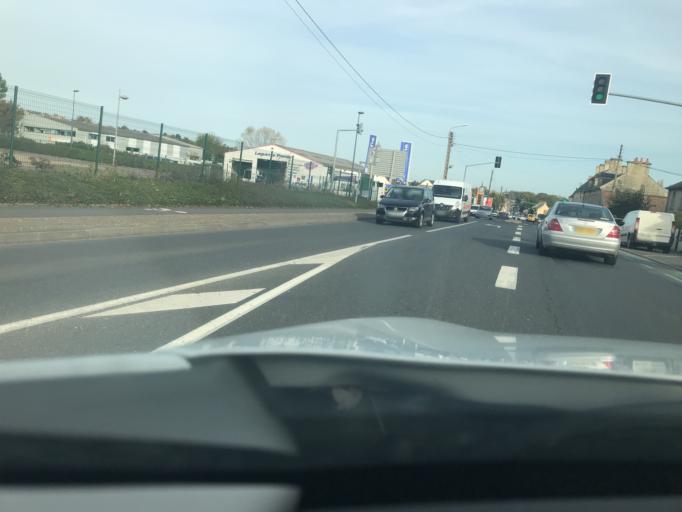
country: FR
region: Lower Normandy
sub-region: Departement du Calvados
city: Bretteville-sur-Odon
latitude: 49.1637
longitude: -0.4230
